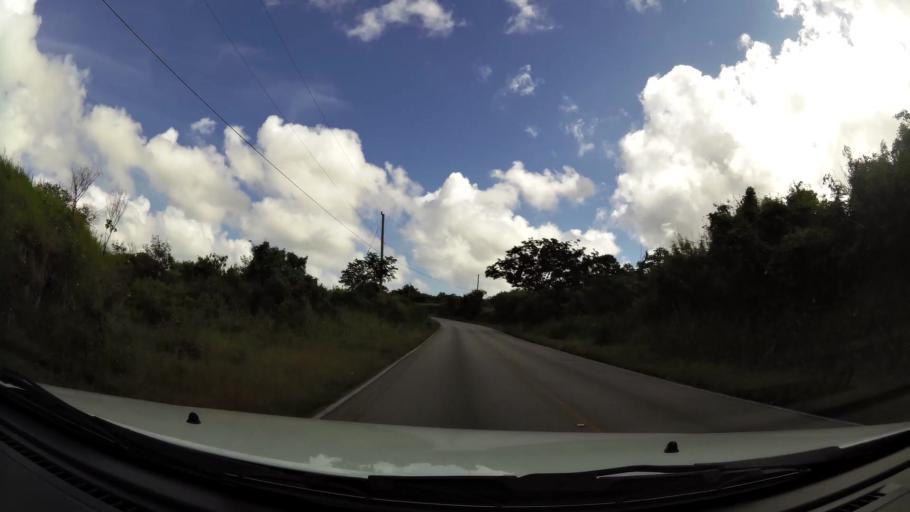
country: BB
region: Saint James
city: Holetown
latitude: 13.1992
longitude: -59.6194
